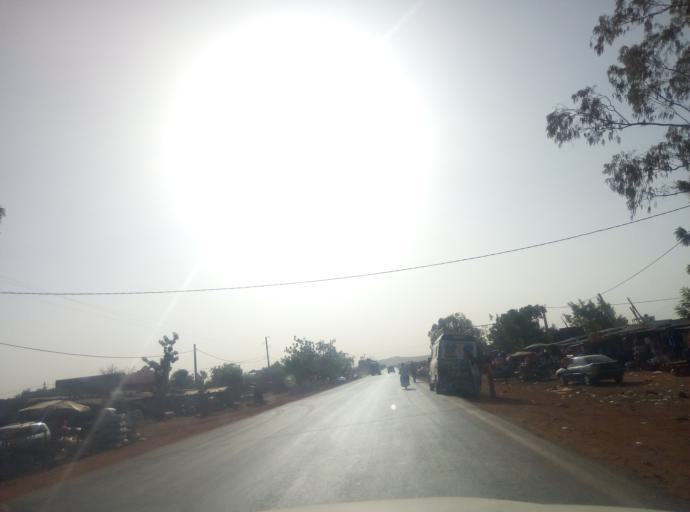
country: ML
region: Bamako
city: Bamako
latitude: 12.5816
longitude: -7.8159
